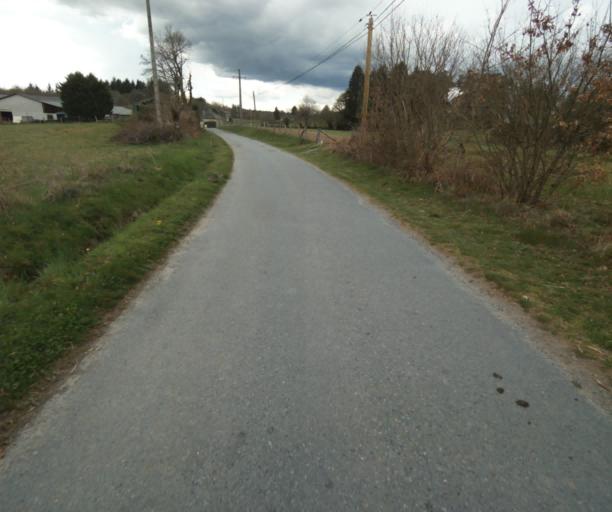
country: FR
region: Limousin
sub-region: Departement de la Correze
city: Correze
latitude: 45.2781
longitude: 1.9490
